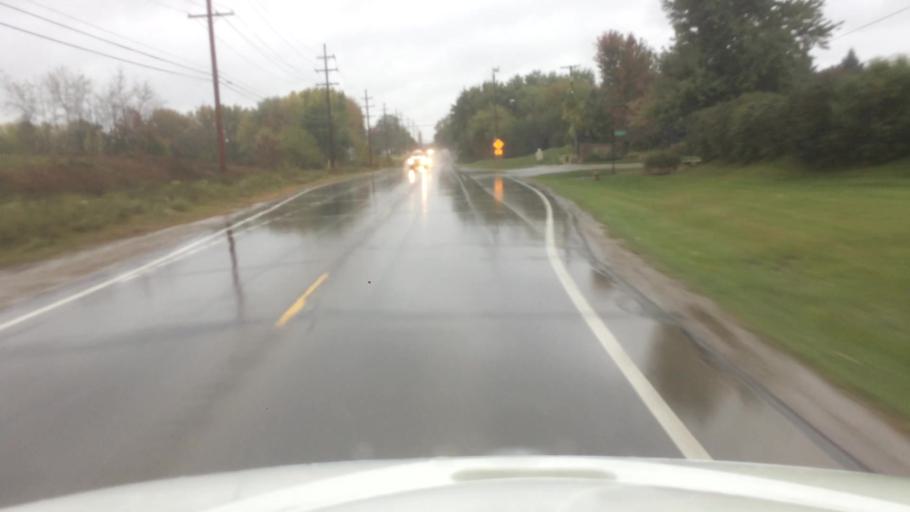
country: US
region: Michigan
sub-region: Oakland County
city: Oxford
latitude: 42.7783
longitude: -83.3195
